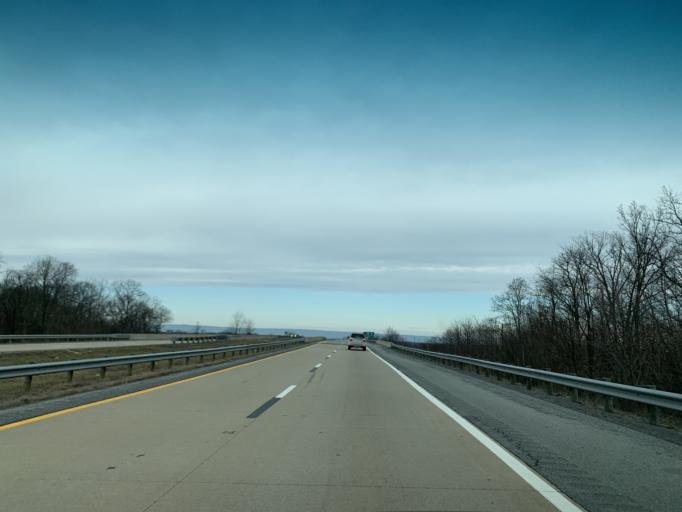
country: US
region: West Virginia
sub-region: Jefferson County
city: Ranson
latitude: 39.3766
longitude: -77.8869
